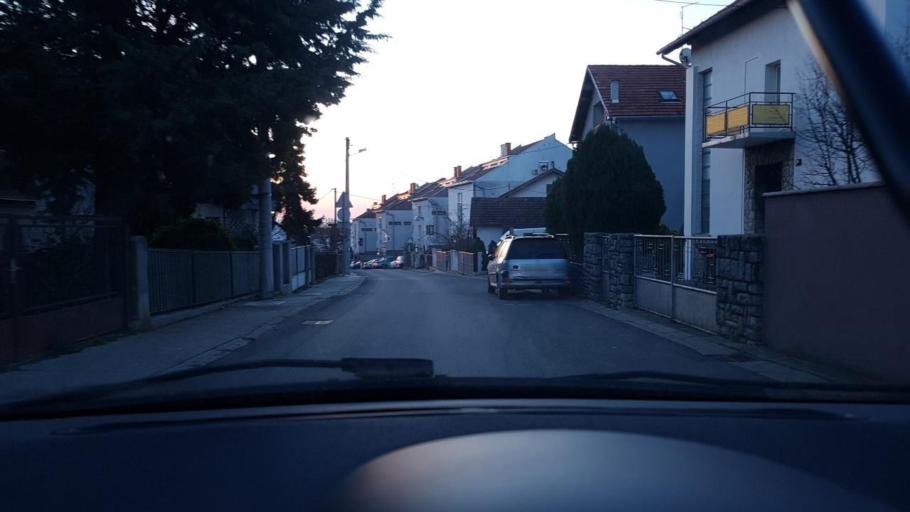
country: HR
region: Grad Zagreb
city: Zagreb
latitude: 45.8318
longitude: 16.0013
